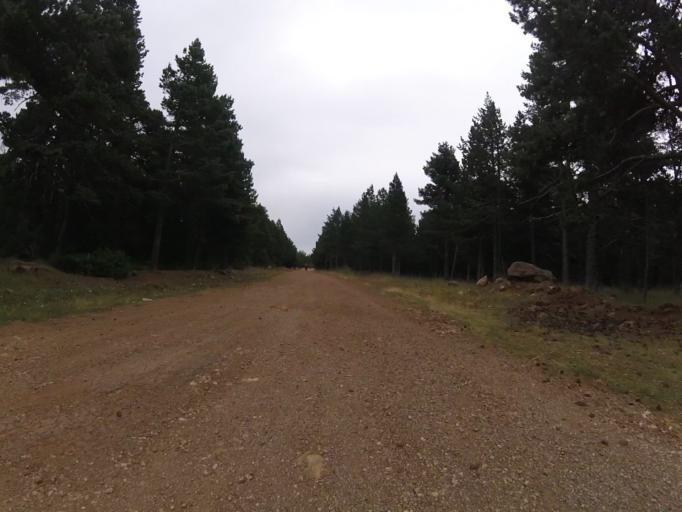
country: ES
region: Aragon
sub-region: Provincia de Teruel
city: Valdelinares
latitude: 40.3727
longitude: -0.6277
